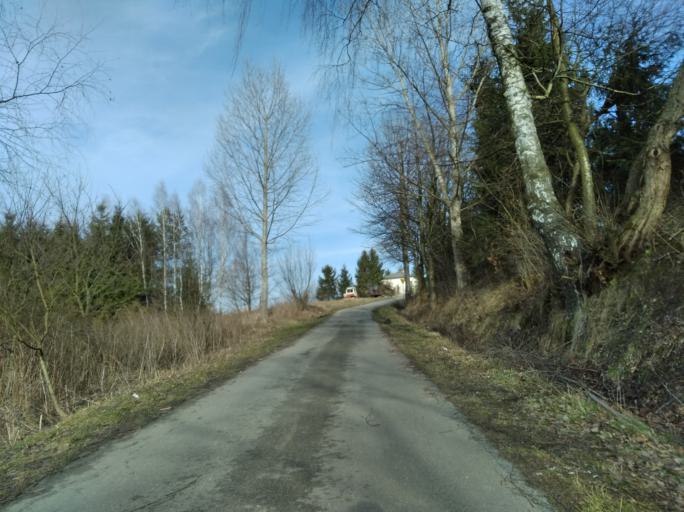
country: PL
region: Subcarpathian Voivodeship
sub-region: Powiat brzozowski
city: Grabownica Starzenska
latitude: 49.6521
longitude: 22.0686
